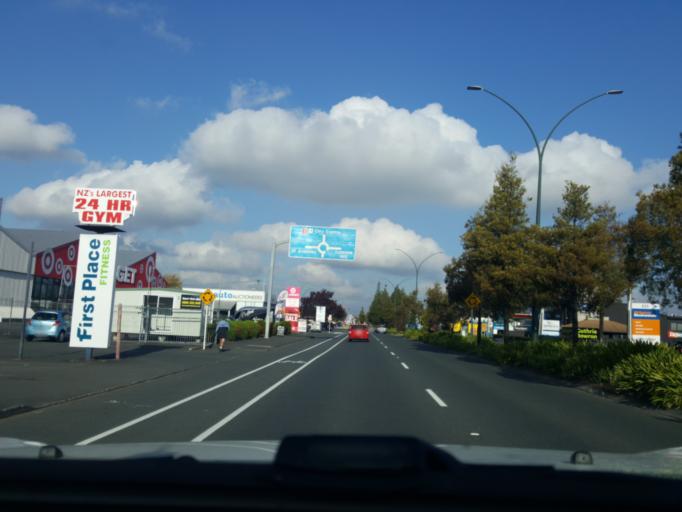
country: NZ
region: Waikato
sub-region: Hamilton City
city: Hamilton
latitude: -37.7564
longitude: 175.2448
